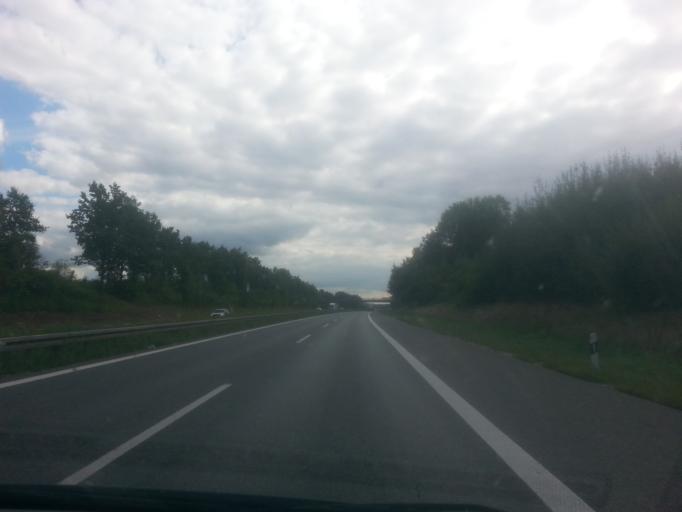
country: DE
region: Bavaria
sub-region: Upper Palatinate
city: Wackersdorf
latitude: 49.3260
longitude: 12.1538
